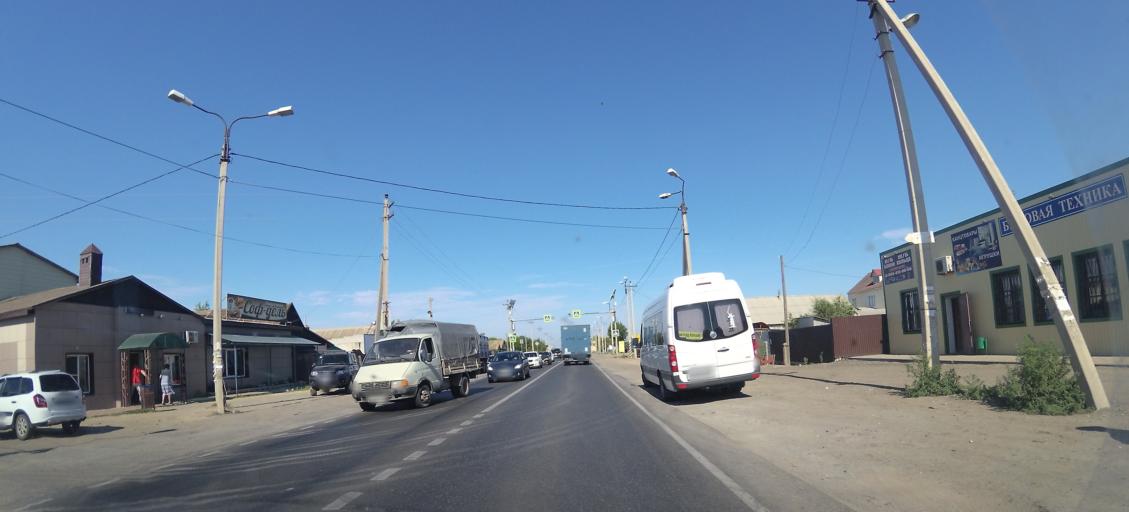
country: RU
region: Volgograd
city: Novyy Rogachik
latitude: 48.6795
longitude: 44.0525
